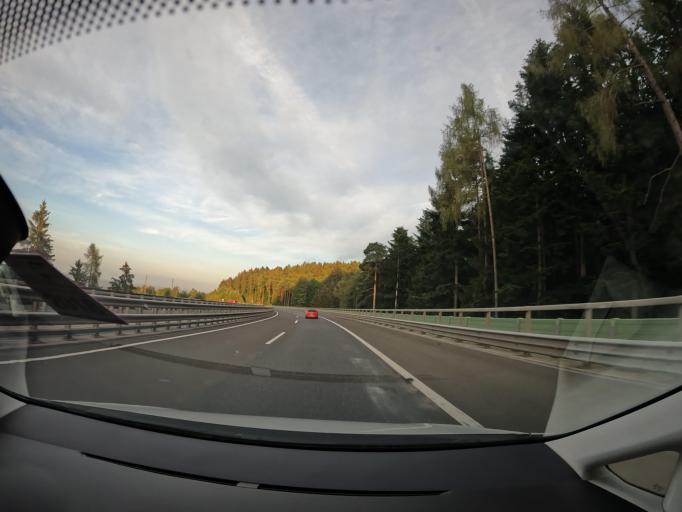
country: AT
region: Styria
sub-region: Politischer Bezirk Voitsberg
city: Ligist
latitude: 46.9746
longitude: 15.1876
